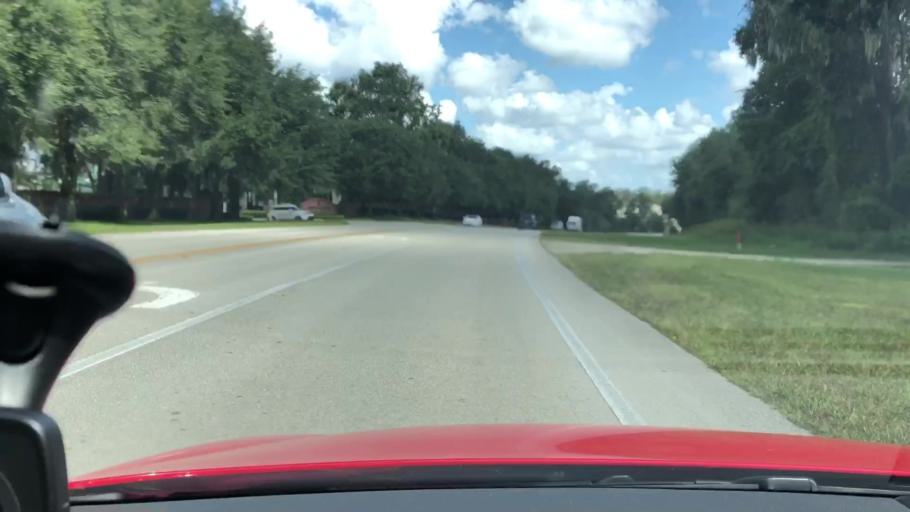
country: US
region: Florida
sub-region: Volusia County
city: Orange City
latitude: 28.9384
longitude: -81.2813
